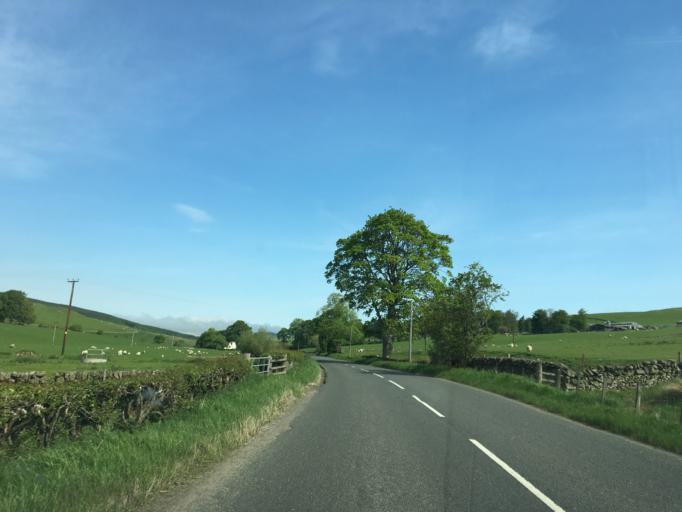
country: GB
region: Scotland
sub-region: South Lanarkshire
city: Biggar
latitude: 55.6229
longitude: -3.4148
